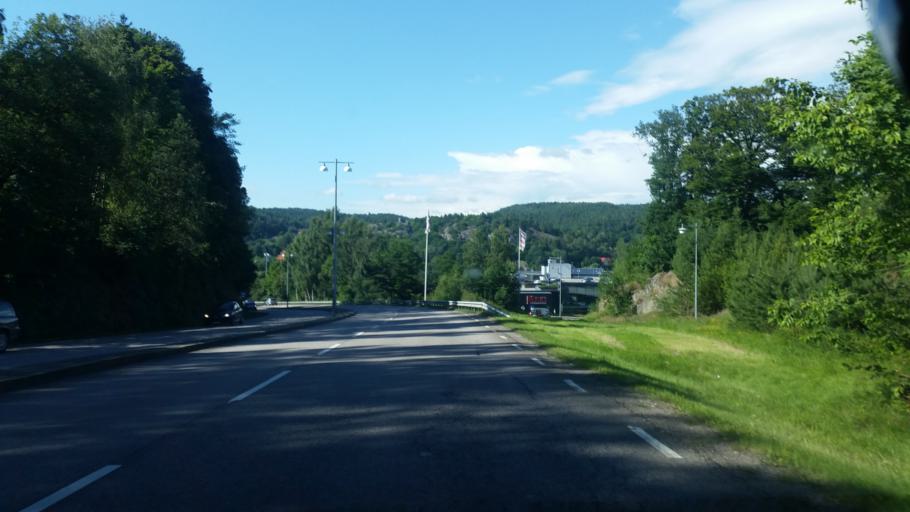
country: SE
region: Vaestra Goetaland
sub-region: Partille Kommun
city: Partille
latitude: 57.7347
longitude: 12.1058
